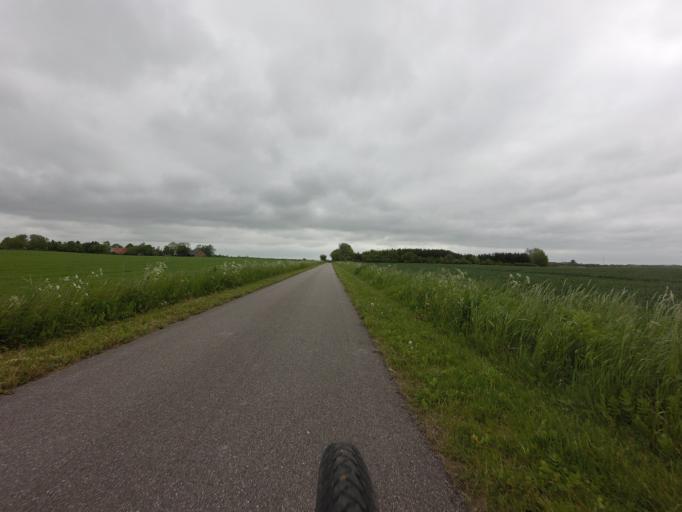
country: DK
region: Zealand
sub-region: Slagelse Kommune
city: Skaelskor
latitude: 55.2539
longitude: 11.3711
